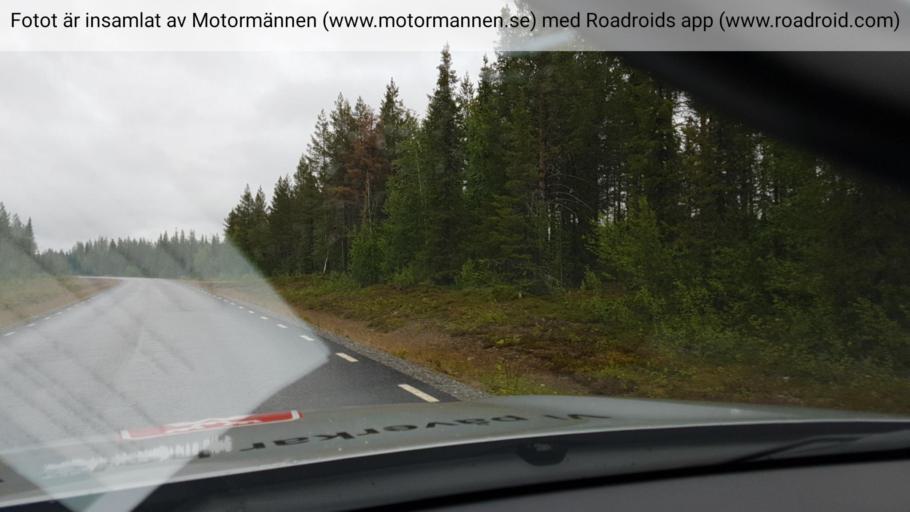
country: SE
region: Norrbotten
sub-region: Gallivare Kommun
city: Gaellivare
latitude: 66.8095
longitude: 21.0433
